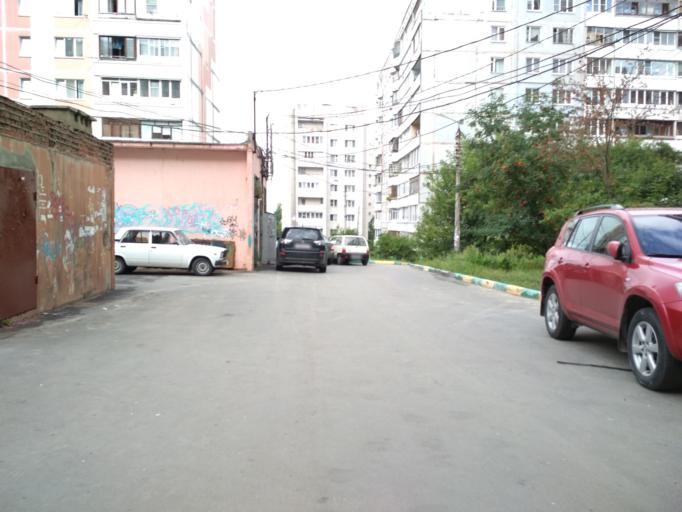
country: RU
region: Tula
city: Mendeleyevskiy
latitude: 54.1552
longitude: 37.5802
